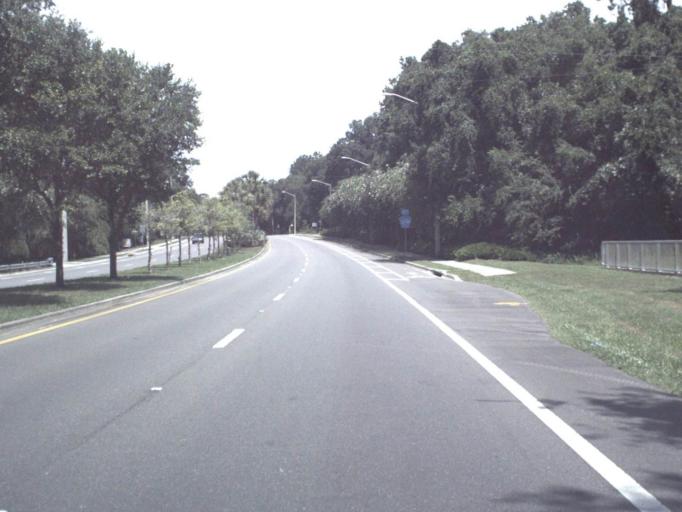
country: US
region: Florida
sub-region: Alachua County
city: Gainesville
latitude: 29.6245
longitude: -82.2579
